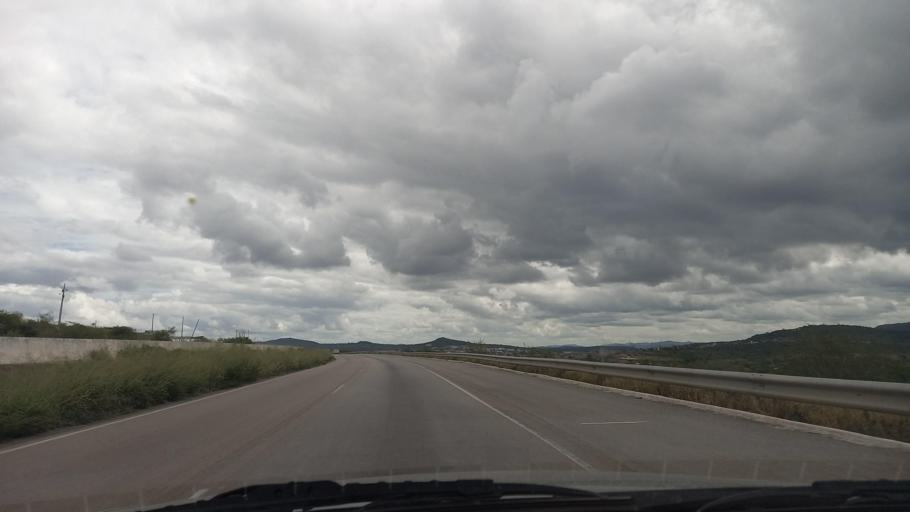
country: BR
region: Pernambuco
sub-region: Caruaru
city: Caruaru
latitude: -8.3241
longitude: -36.1092
